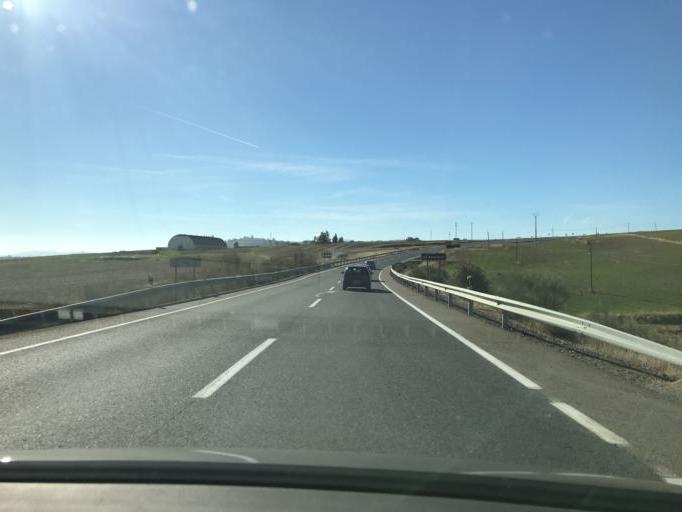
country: ES
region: Extremadura
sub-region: Provincia de Badajoz
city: Azuaga
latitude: 38.2802
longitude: -5.6616
